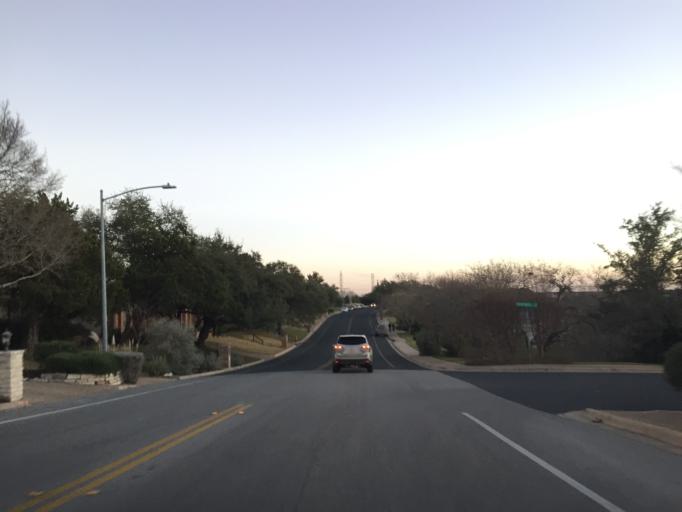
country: US
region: Texas
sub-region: Williamson County
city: Jollyville
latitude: 30.4054
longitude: -97.7691
